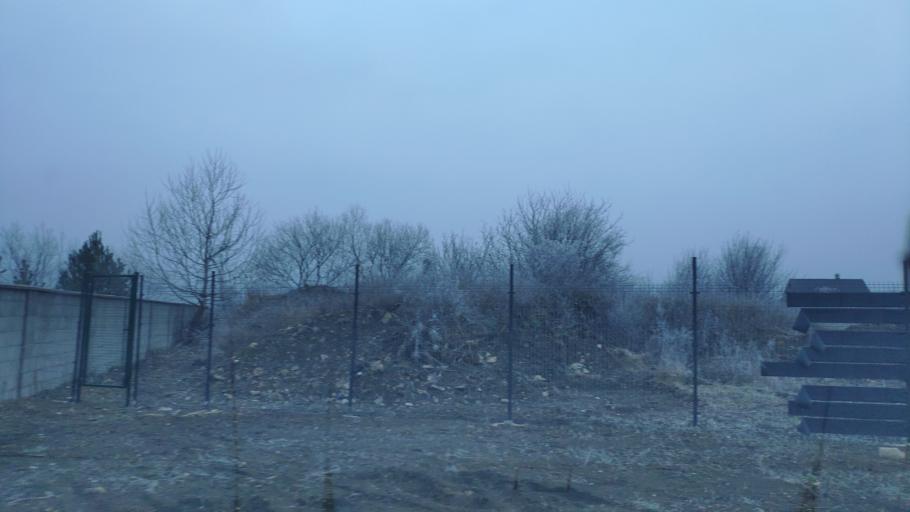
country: SK
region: Kosicky
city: Kosice
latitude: 48.6166
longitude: 21.3273
